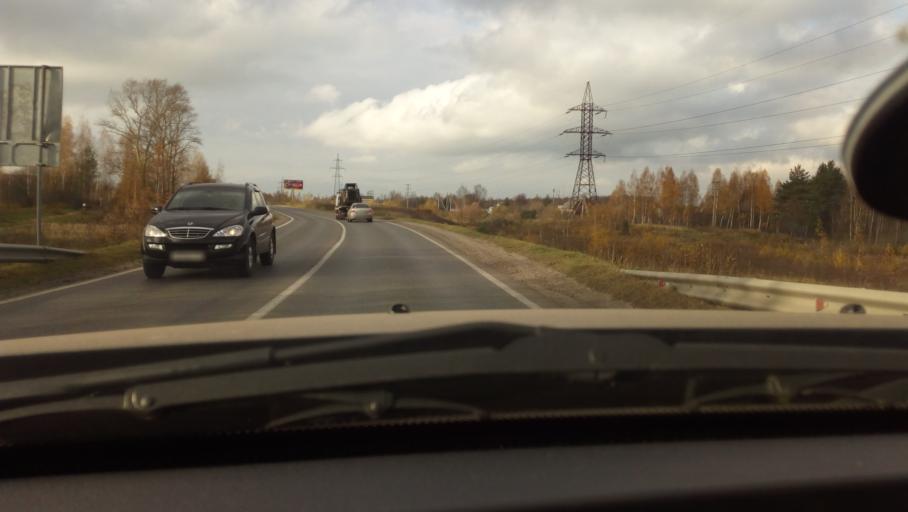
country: RU
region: Moskovskaya
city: Pavlovskiy Posad
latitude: 55.7532
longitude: 38.6518
